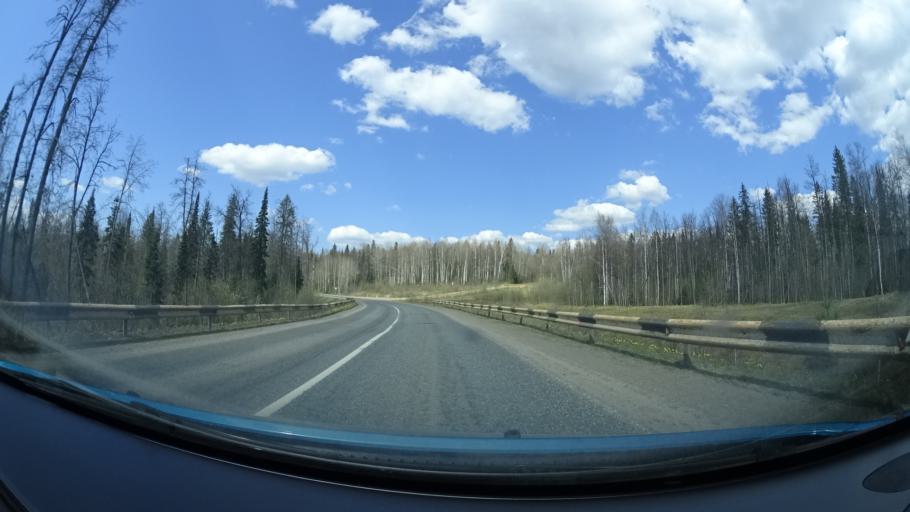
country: RU
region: Perm
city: Yugo-Kamskiy
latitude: 57.6041
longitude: 55.6561
